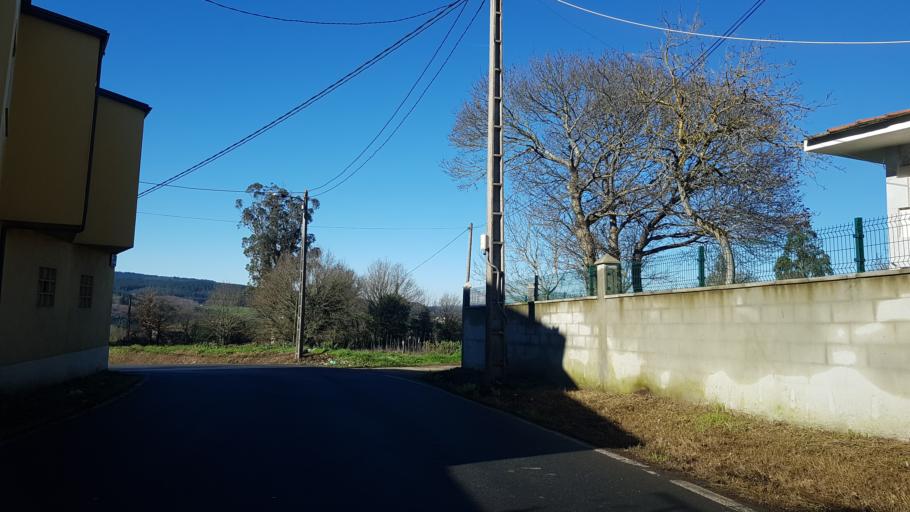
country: ES
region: Galicia
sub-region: Provincia de Lugo
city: Lugo
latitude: 43.0185
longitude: -7.5791
